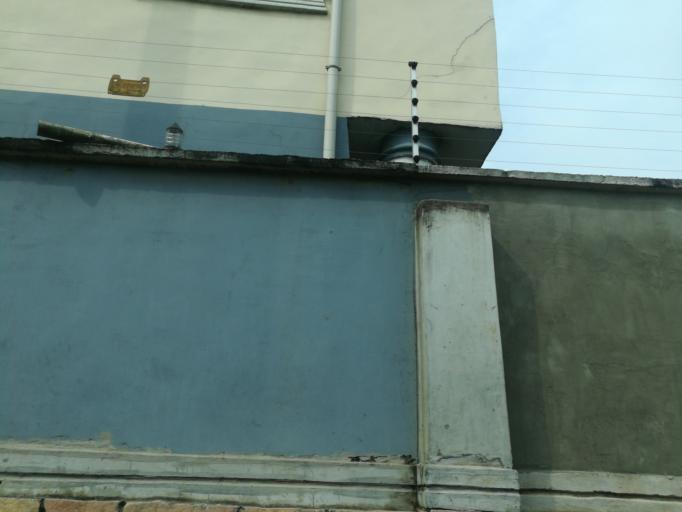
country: NG
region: Rivers
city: Port Harcourt
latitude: 4.8709
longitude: 6.9837
